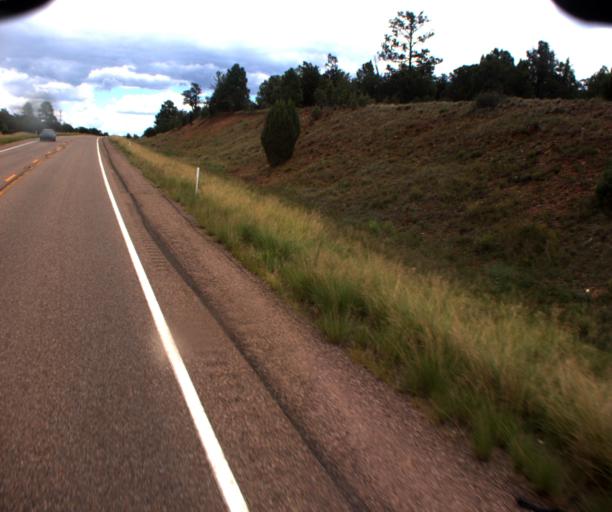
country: US
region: Arizona
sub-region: Navajo County
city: Linden
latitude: 34.3418
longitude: -110.2831
